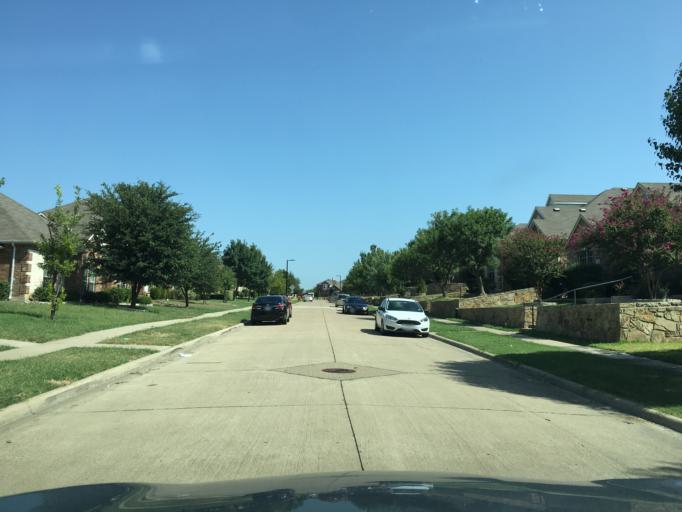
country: US
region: Texas
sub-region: Dallas County
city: Garland
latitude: 32.8910
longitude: -96.6113
